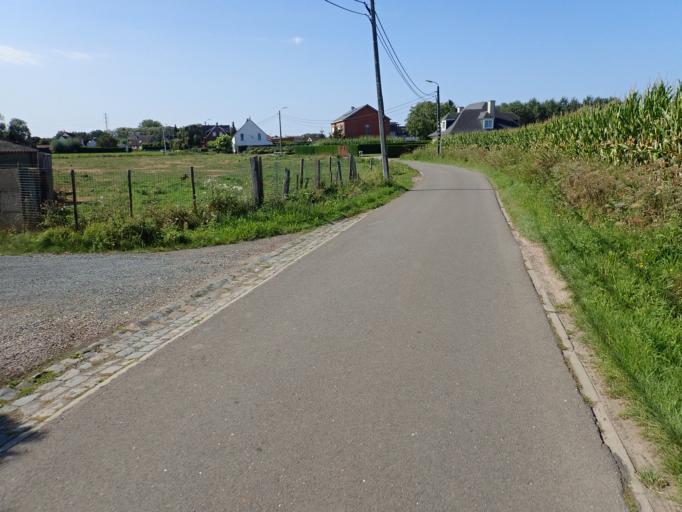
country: BE
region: Flanders
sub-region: Provincie Antwerpen
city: Puurs
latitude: 51.0499
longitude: 4.3052
